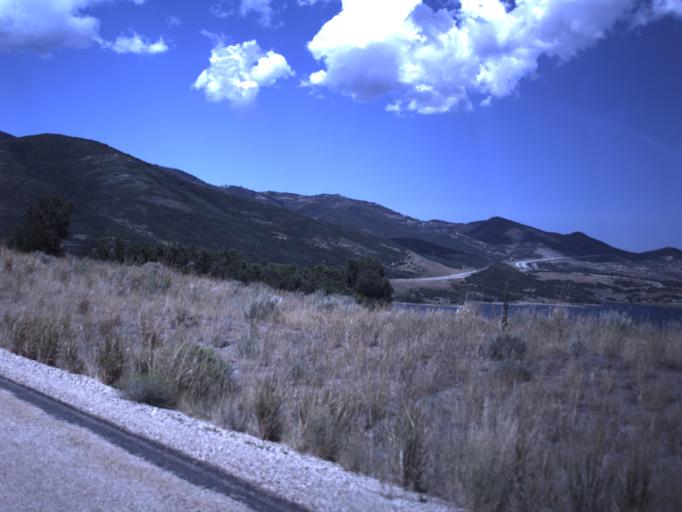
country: US
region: Utah
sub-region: Wasatch County
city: Heber
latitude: 40.5946
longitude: -111.4103
